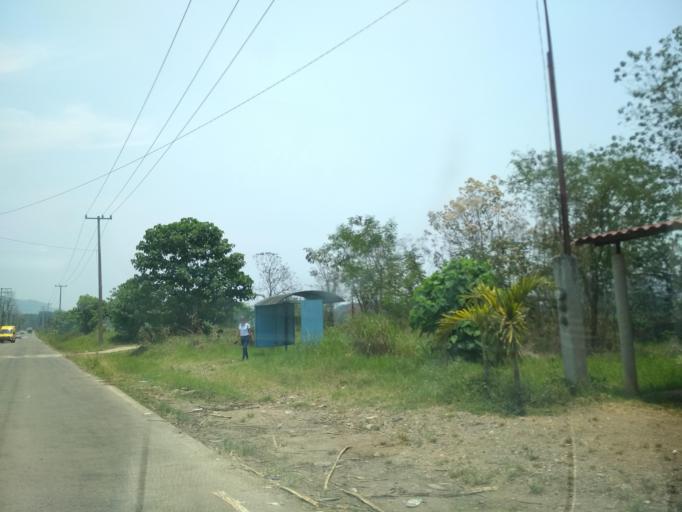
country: MX
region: Veracruz
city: Cosolapa
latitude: 18.5878
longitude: -96.6983
